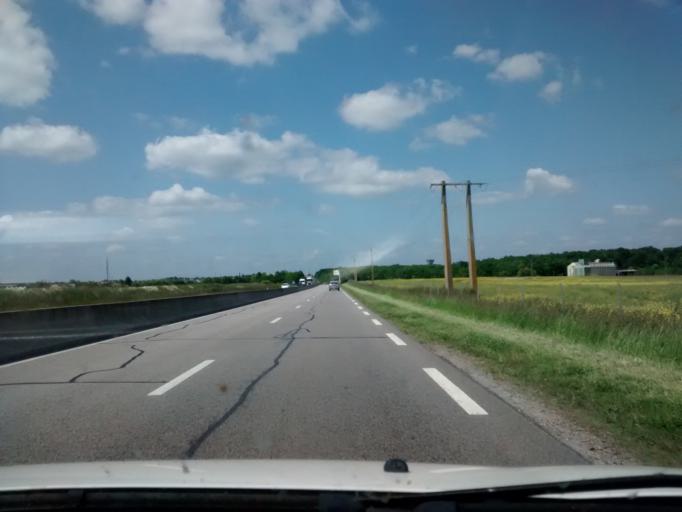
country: FR
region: Ile-de-France
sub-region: Departement des Yvelines
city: Rambouillet
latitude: 48.6148
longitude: 1.8315
